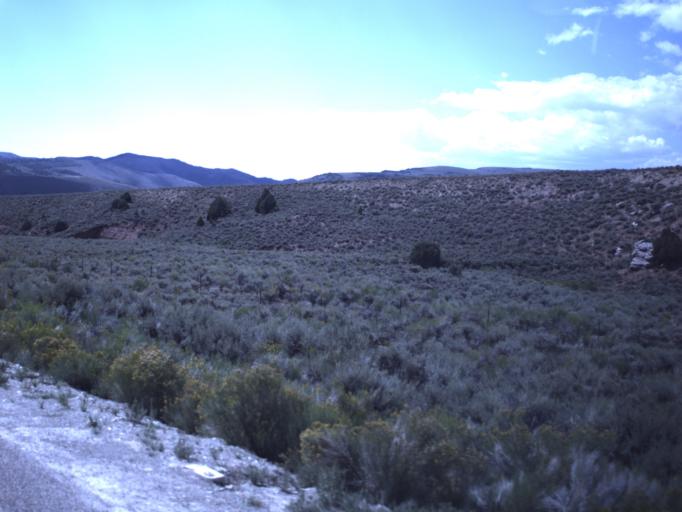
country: US
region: Utah
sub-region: Carbon County
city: Helper
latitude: 39.8167
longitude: -110.7815
